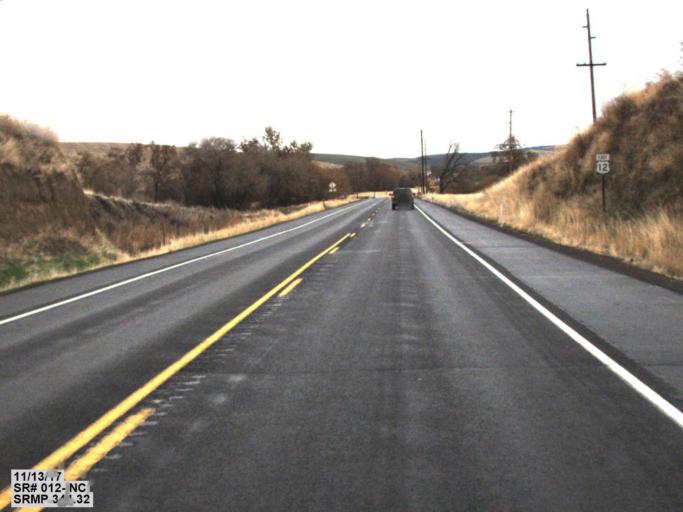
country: US
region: Washington
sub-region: Walla Walla County
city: Walla Walla East
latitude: 46.1172
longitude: -118.2192
